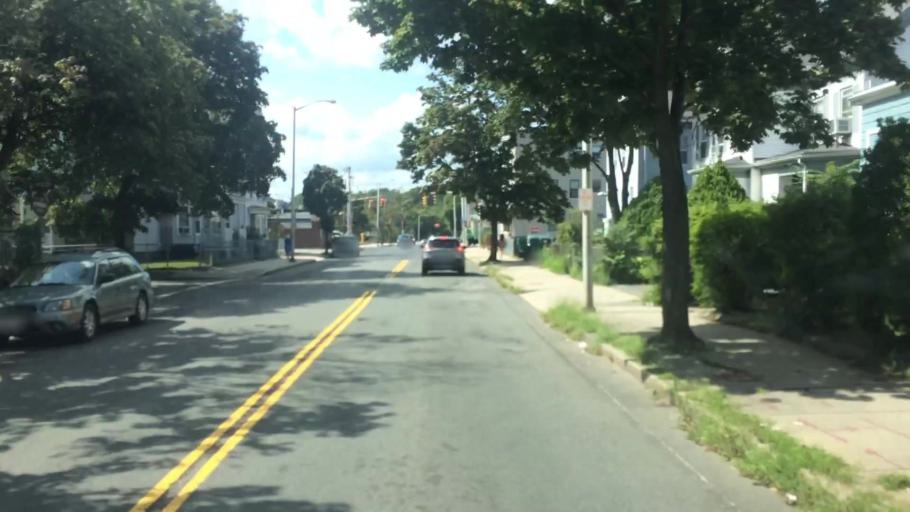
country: US
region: Massachusetts
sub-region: Essex County
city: Lynn
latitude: 42.4692
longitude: -70.9559
